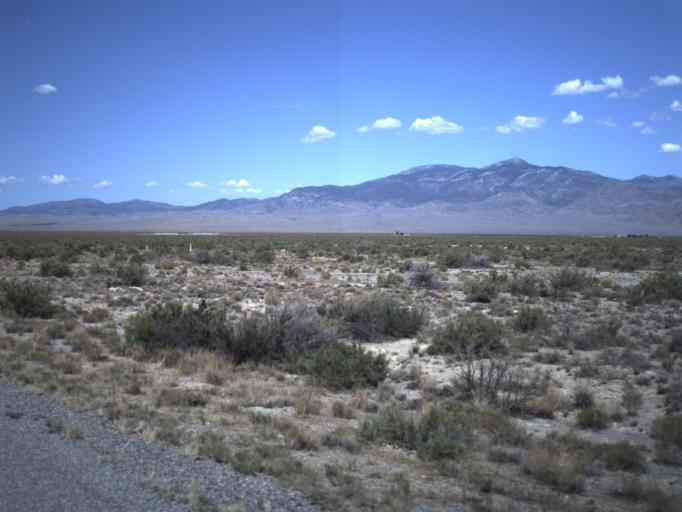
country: US
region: Nevada
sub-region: White Pine County
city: McGill
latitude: 39.0546
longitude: -114.0149
